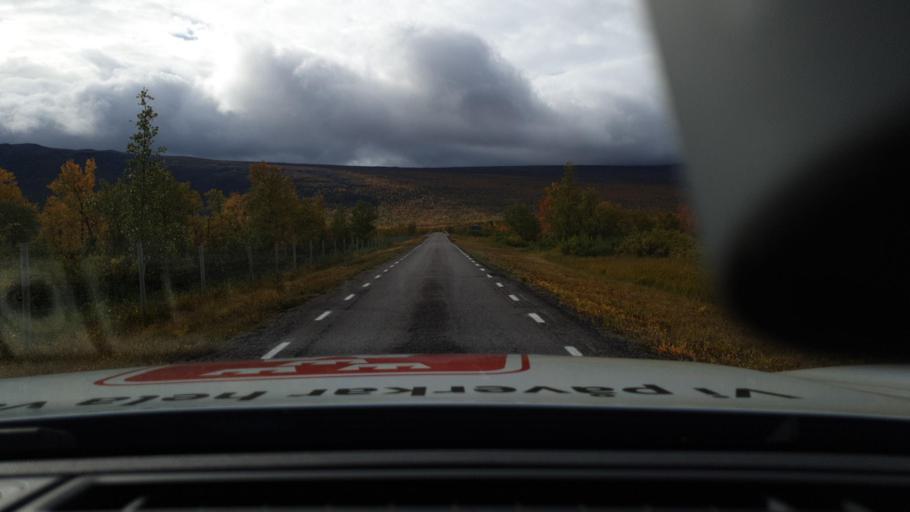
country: SE
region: Norrbotten
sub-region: Kiruna Kommun
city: Kiruna
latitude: 67.8580
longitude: 19.0246
